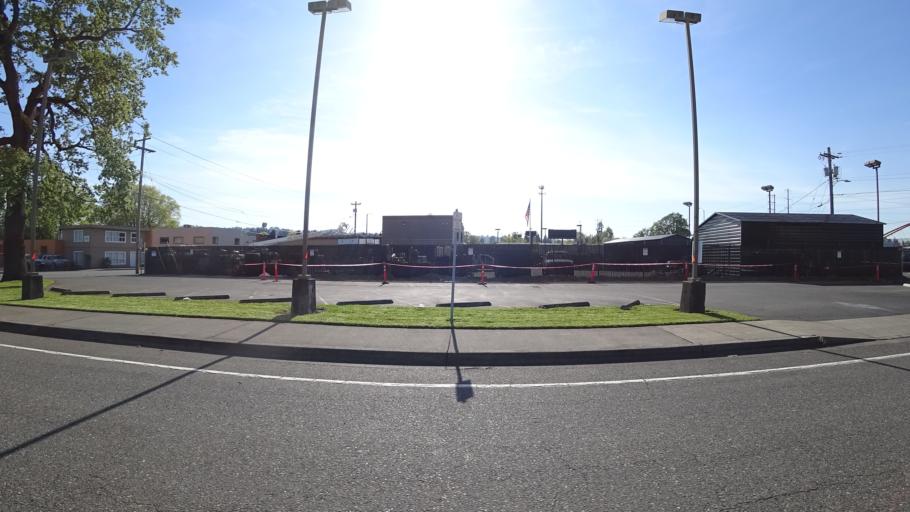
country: US
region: Oregon
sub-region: Clackamas County
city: Milwaukie
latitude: 45.4591
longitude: -122.6383
